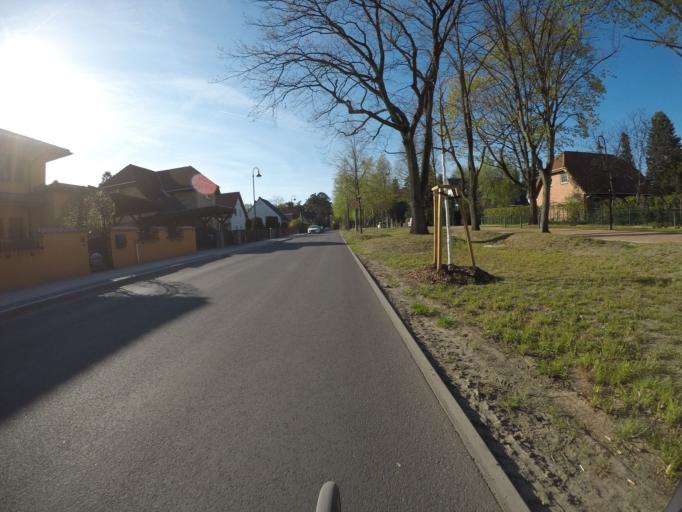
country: DE
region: Brandenburg
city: Neuenhagen
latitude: 52.5135
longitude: 13.6988
